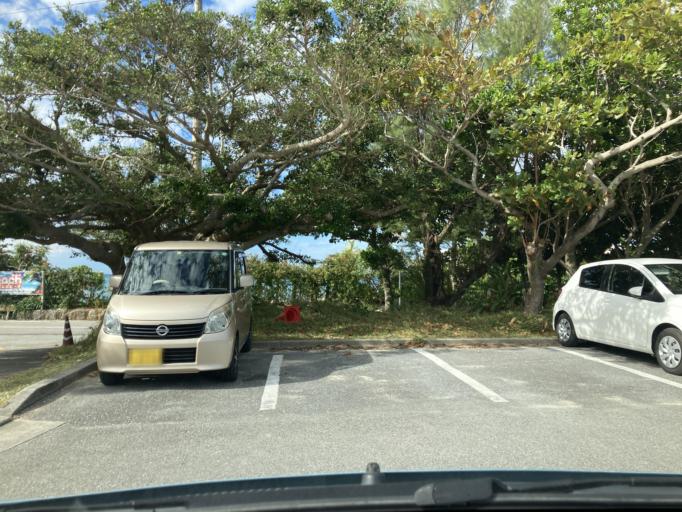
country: JP
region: Okinawa
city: Ishikawa
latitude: 26.4361
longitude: 127.7167
